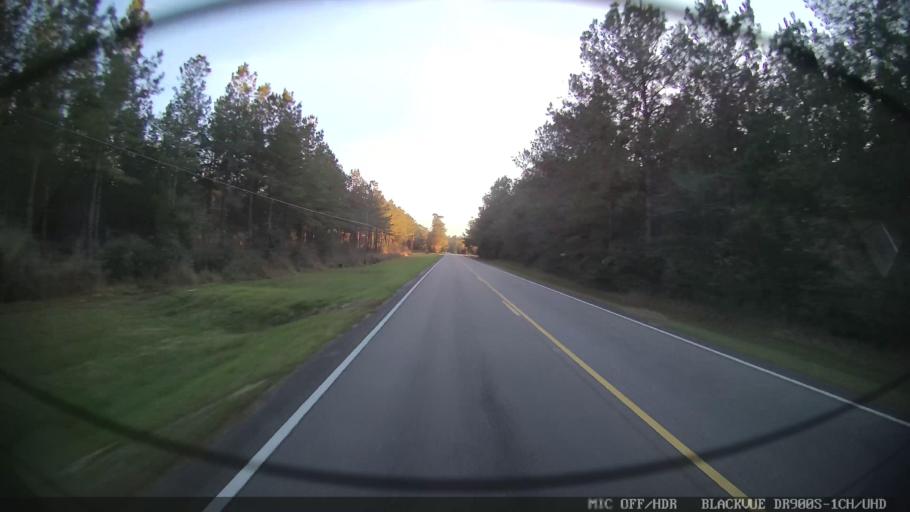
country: US
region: Mississippi
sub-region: Lamar County
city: Lumberton
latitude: 31.0156
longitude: -89.2551
